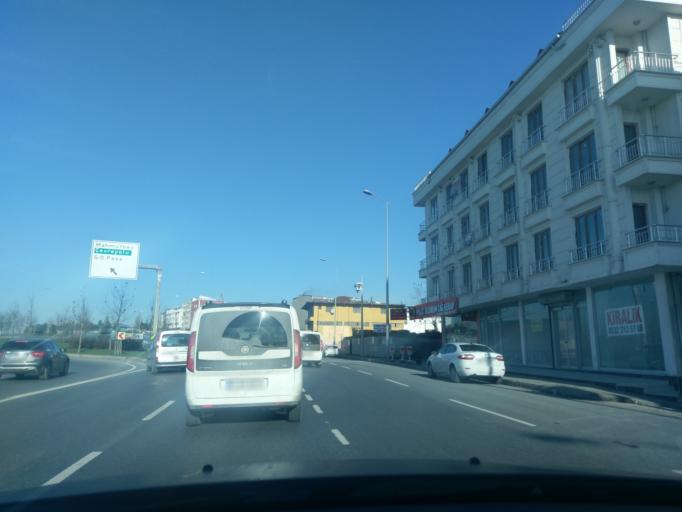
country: TR
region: Istanbul
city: Sultangazi
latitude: 41.1098
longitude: 28.8490
